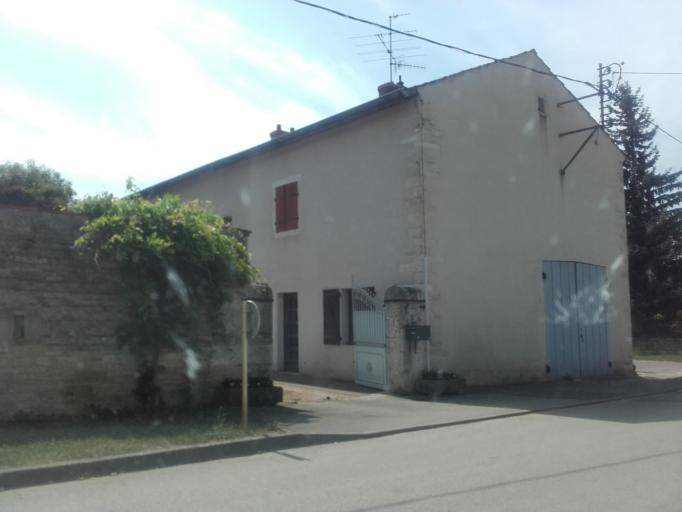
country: FR
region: Bourgogne
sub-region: Departement de Saone-et-Loire
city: Demigny
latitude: 46.9321
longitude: 4.8358
